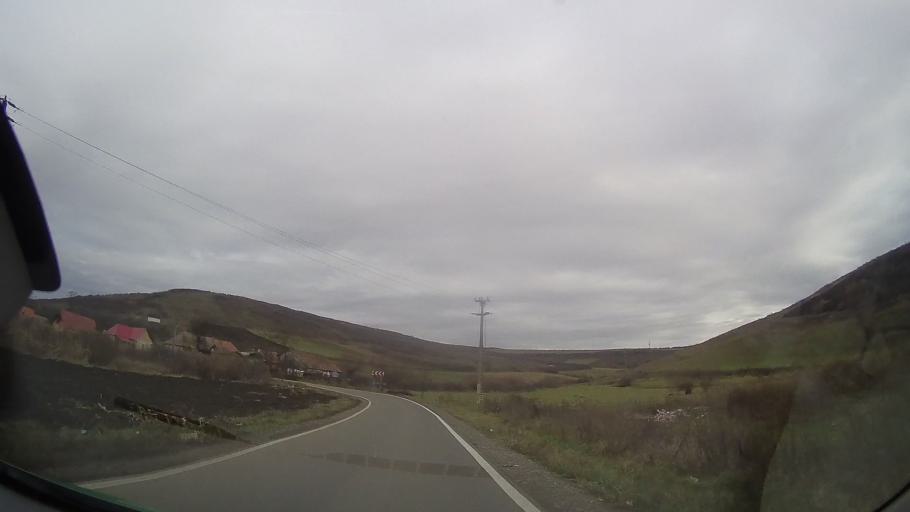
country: RO
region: Mures
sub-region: Comuna Faragau
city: Faragau
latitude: 46.7746
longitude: 24.5590
